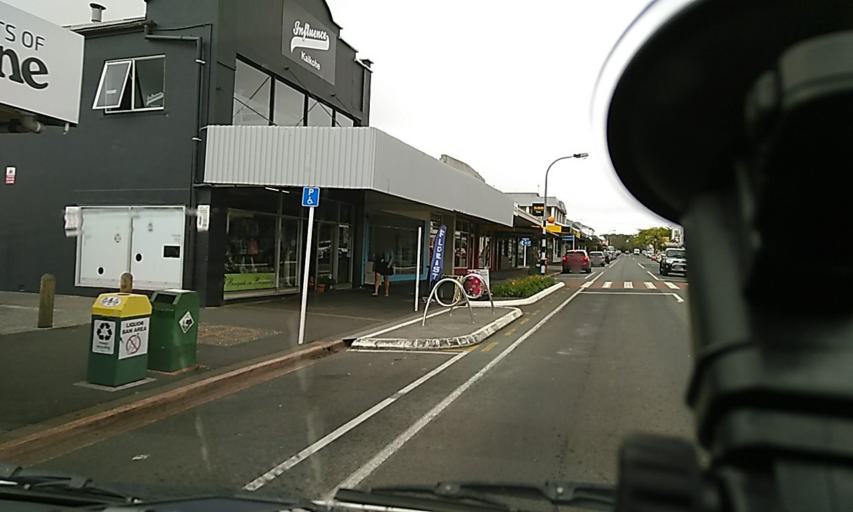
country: NZ
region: Northland
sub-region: Far North District
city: Waimate North
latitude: -35.4076
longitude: 173.7999
